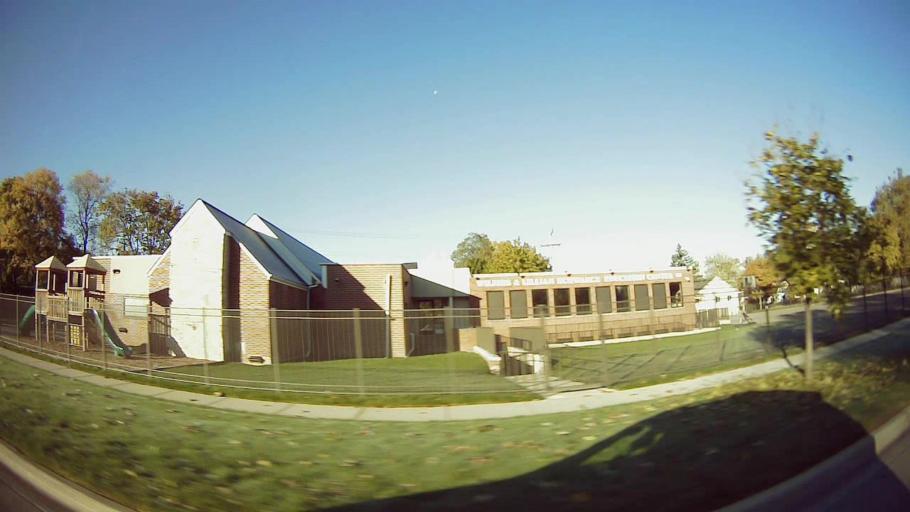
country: US
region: Michigan
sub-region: Oakland County
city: Huntington Woods
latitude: 42.4782
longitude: -83.1829
